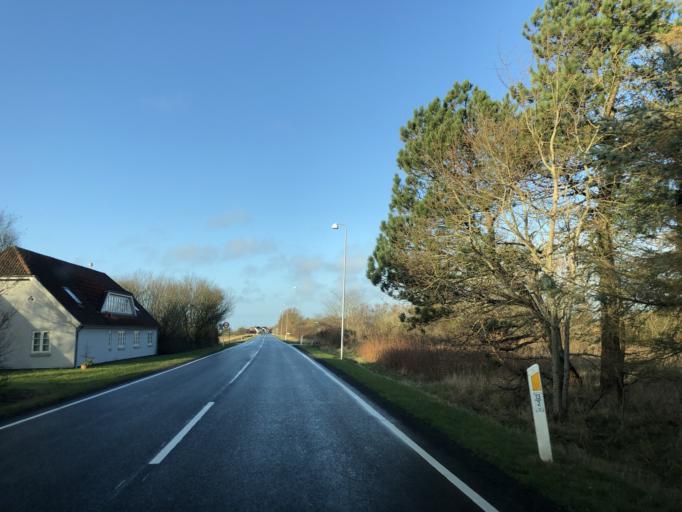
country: DK
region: Central Jutland
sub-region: Struer Kommune
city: Struer
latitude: 56.5462
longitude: 8.4951
